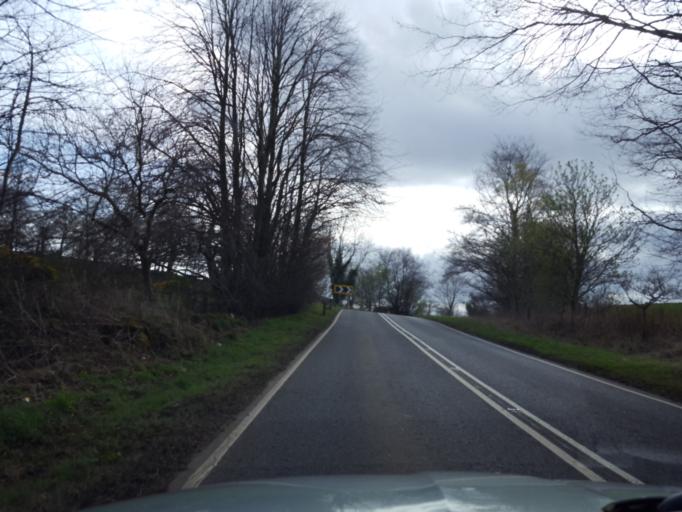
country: GB
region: Scotland
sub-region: West Lothian
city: Bathgate
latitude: 55.9546
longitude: -3.6596
